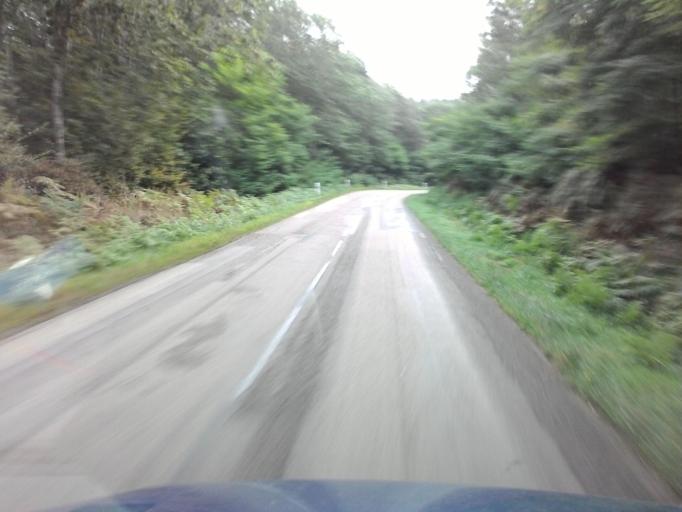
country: FR
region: Bourgogne
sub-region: Departement de la Nievre
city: Chateau-Chinon(Ville)
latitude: 47.0869
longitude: 3.9214
